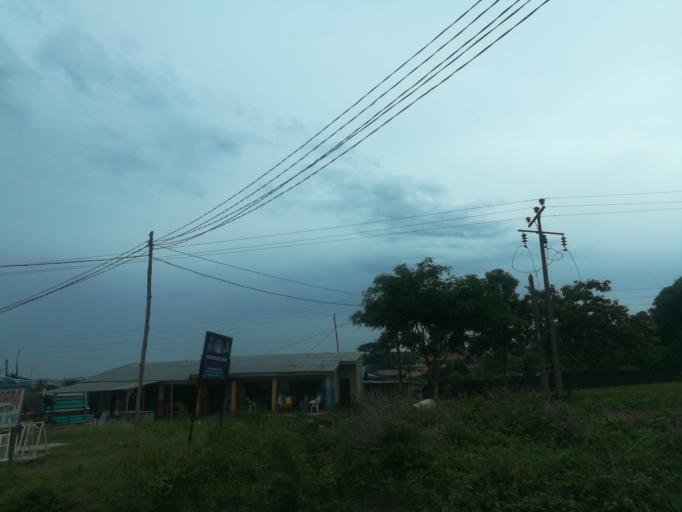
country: NG
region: Oyo
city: Egbeda
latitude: 7.3851
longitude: 4.0006
